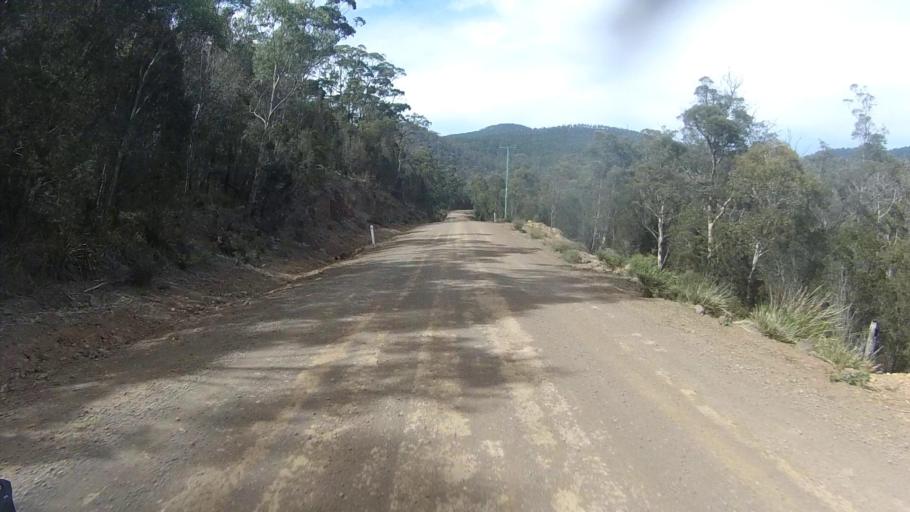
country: AU
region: Tasmania
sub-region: Sorell
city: Sorell
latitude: -42.6744
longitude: 147.8835
